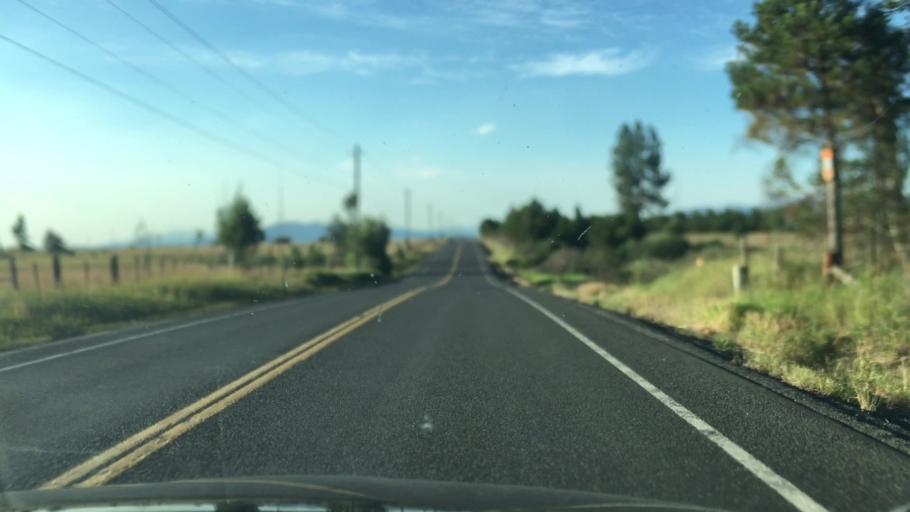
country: US
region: Idaho
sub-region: Valley County
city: McCall
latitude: 44.7963
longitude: -116.0782
